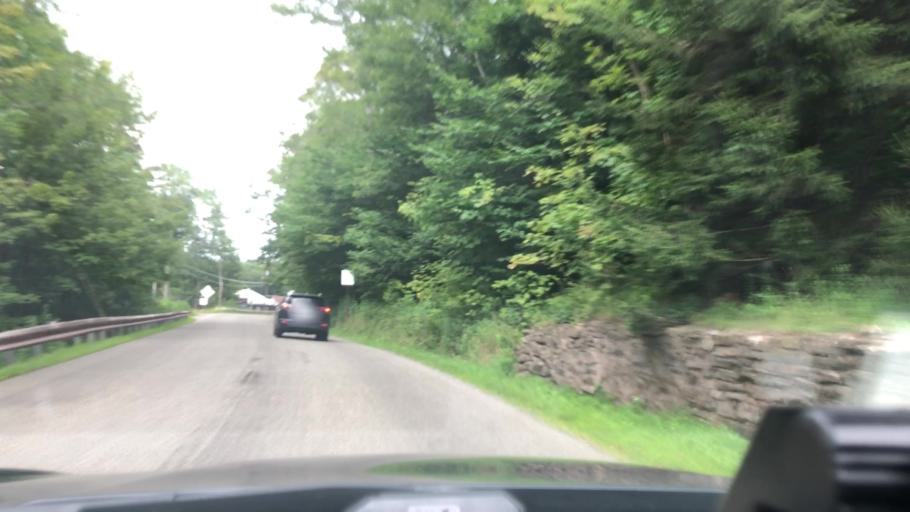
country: US
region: Pennsylvania
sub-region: Lackawanna County
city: Moscow
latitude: 41.2424
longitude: -75.4830
